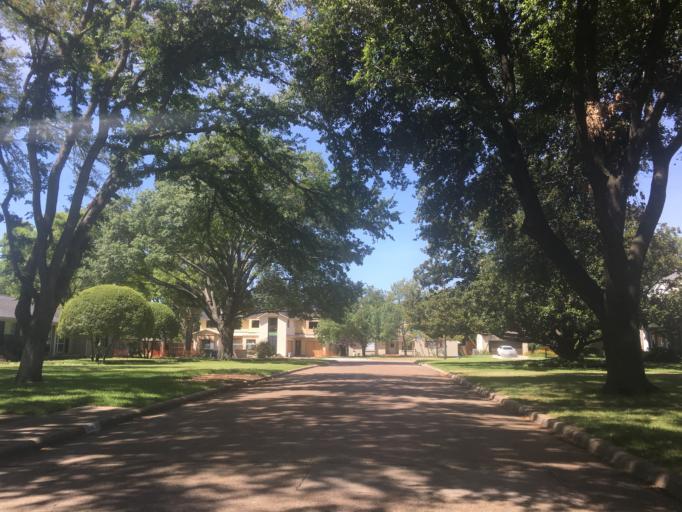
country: US
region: Texas
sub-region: Dallas County
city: Highland Park
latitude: 32.8691
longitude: -96.7232
